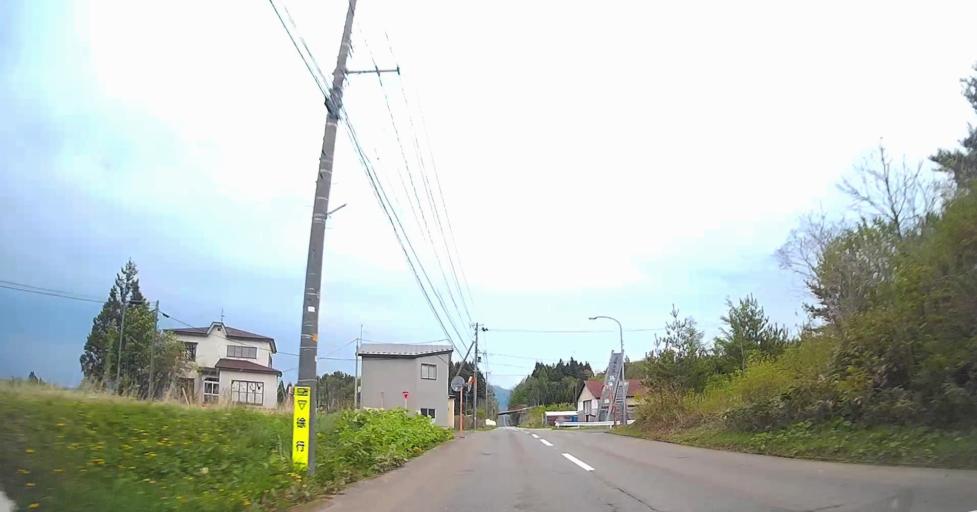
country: JP
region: Aomori
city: Shimokizukuri
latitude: 41.1789
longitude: 140.4682
